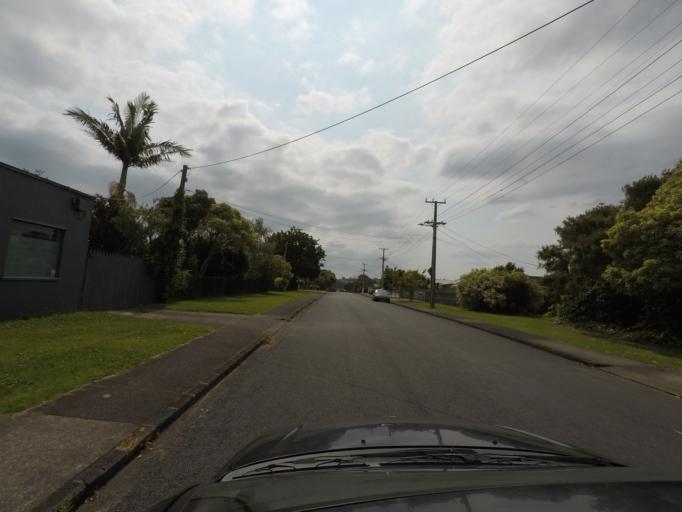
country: NZ
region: Auckland
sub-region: Auckland
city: Rosebank
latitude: -36.8313
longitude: 174.6461
